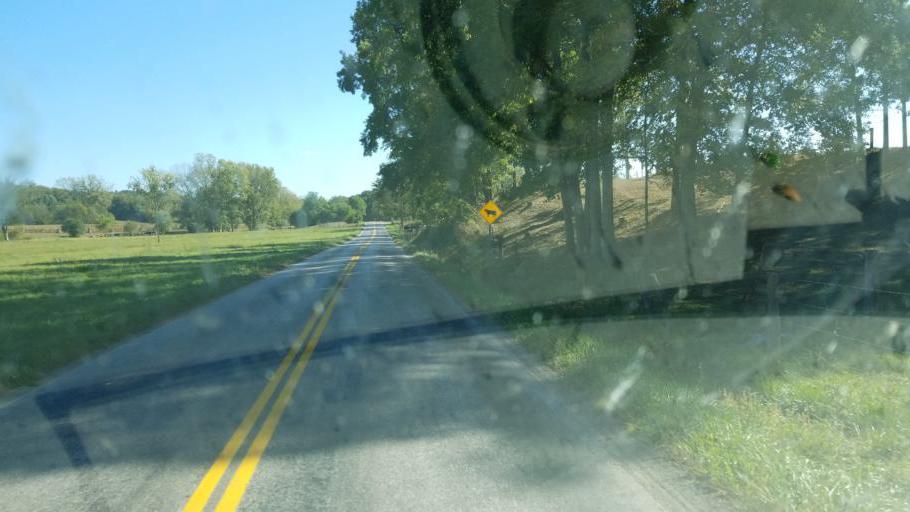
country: US
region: Ohio
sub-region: Wayne County
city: West Salem
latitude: 40.9129
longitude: -82.1621
